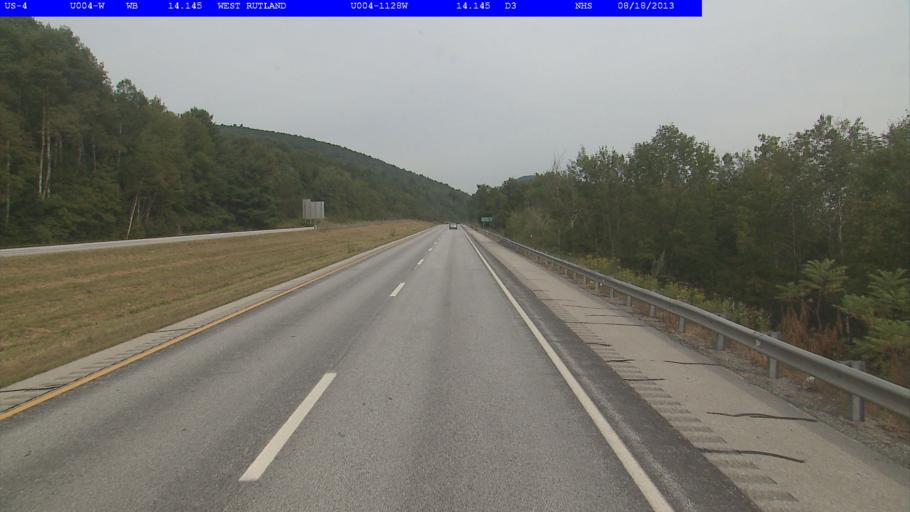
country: US
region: Vermont
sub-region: Rutland County
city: West Rutland
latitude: 43.5916
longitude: -73.0516
